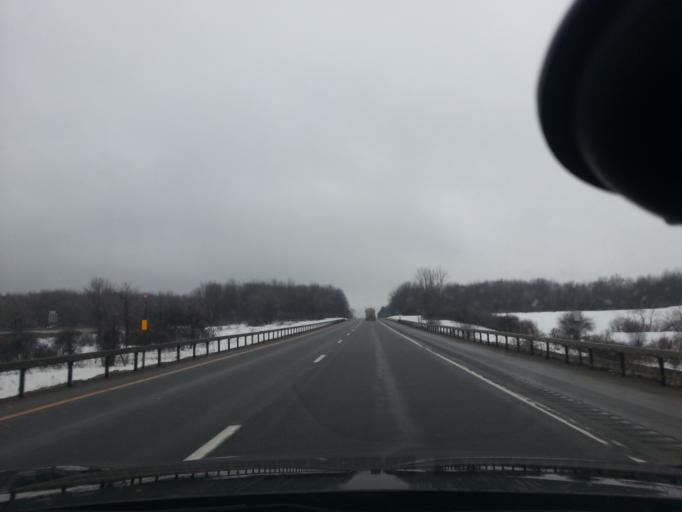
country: US
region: New York
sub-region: Oswego County
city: Pulaski
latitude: 43.5375
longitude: -76.1173
